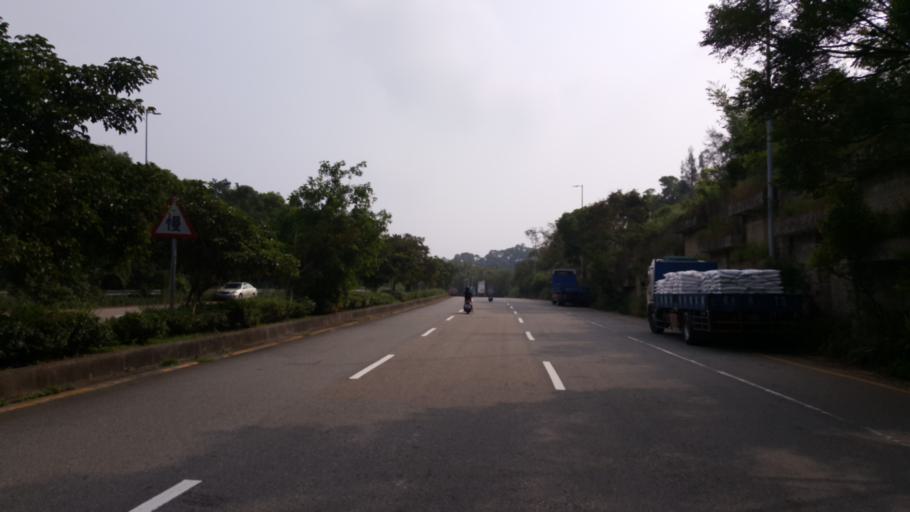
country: TW
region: Taiwan
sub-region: Hsinchu
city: Hsinchu
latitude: 24.7519
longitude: 120.9557
